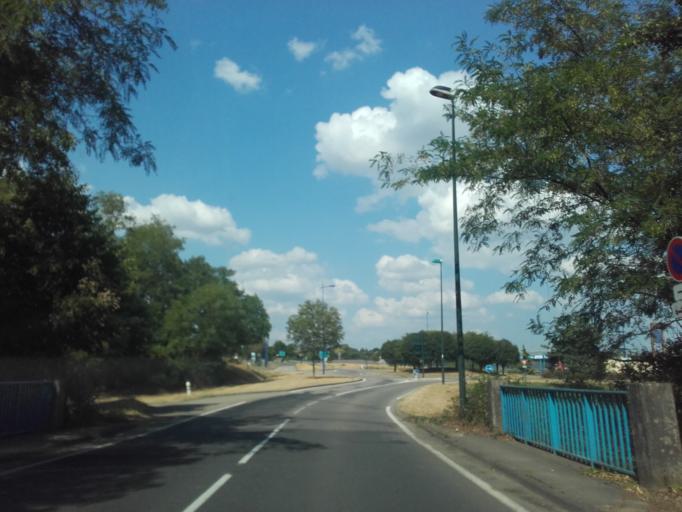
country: FR
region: Bourgogne
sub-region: Departement de Saone-et-Loire
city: Charnay-les-Macon
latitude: 46.2845
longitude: 4.7805
